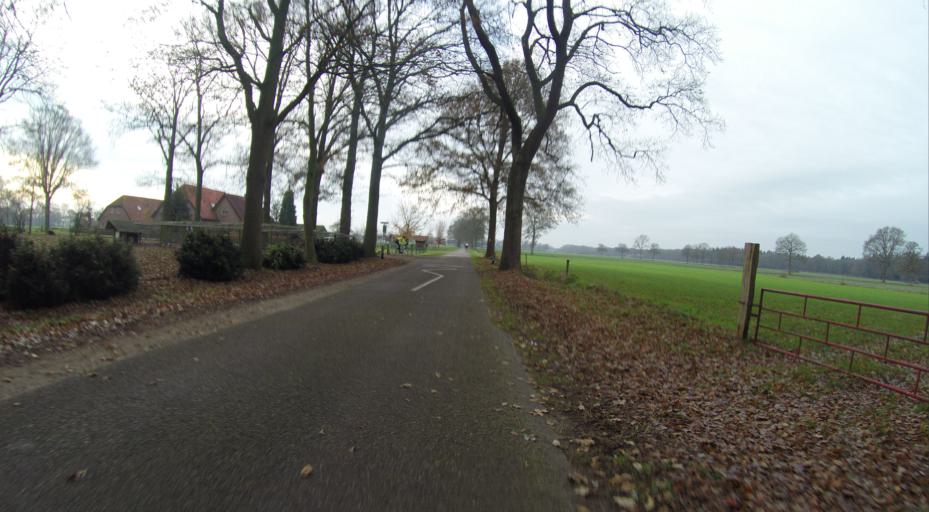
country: NL
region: Gelderland
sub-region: Gemeente Lochem
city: Lochem
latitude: 52.1481
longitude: 6.4049
